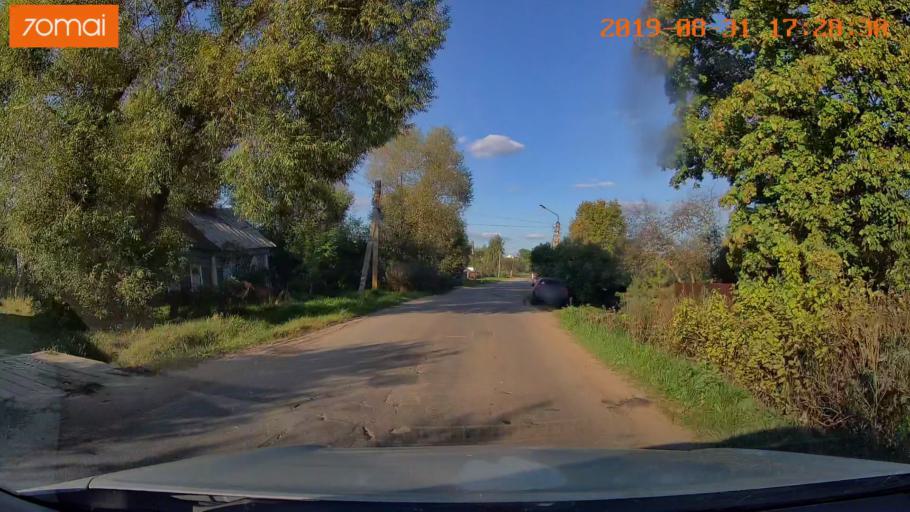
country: RU
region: Kaluga
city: Detchino
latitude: 54.8125
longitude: 36.3183
